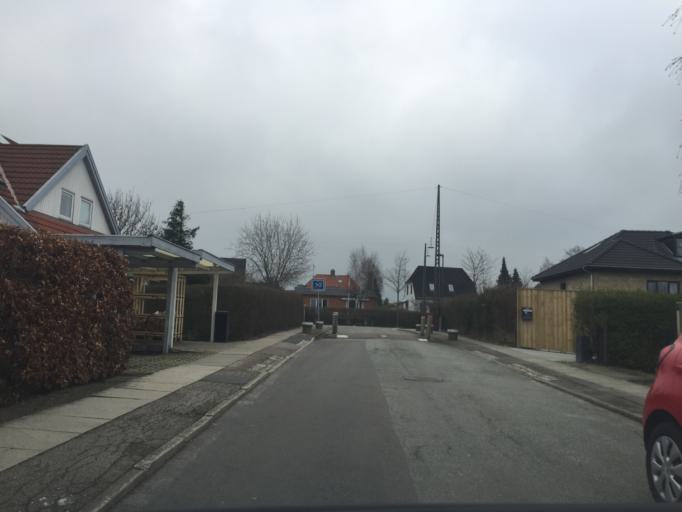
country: DK
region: Capital Region
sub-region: Tarnby Kommune
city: Tarnby
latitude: 55.6417
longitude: 12.5979
